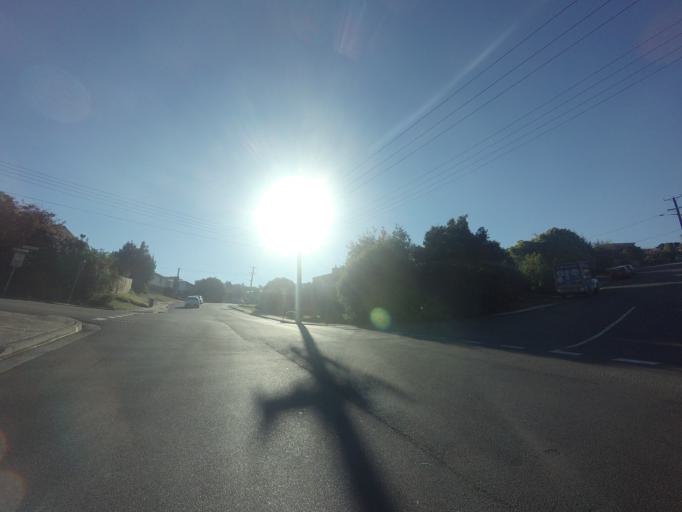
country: AU
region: Tasmania
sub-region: Glenorchy
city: West Moonah
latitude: -42.8624
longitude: 147.2818
